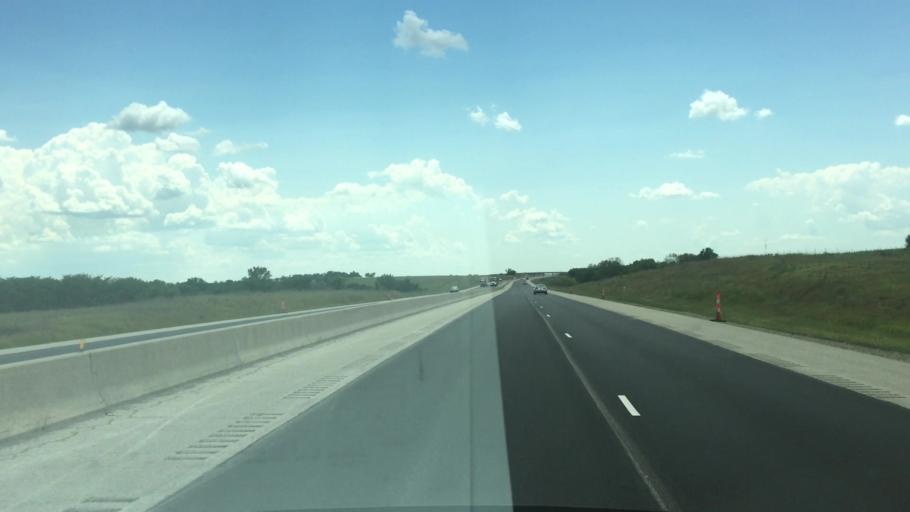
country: US
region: Kansas
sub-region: Lyon County
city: Emporia
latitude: 38.5819
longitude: -96.0876
